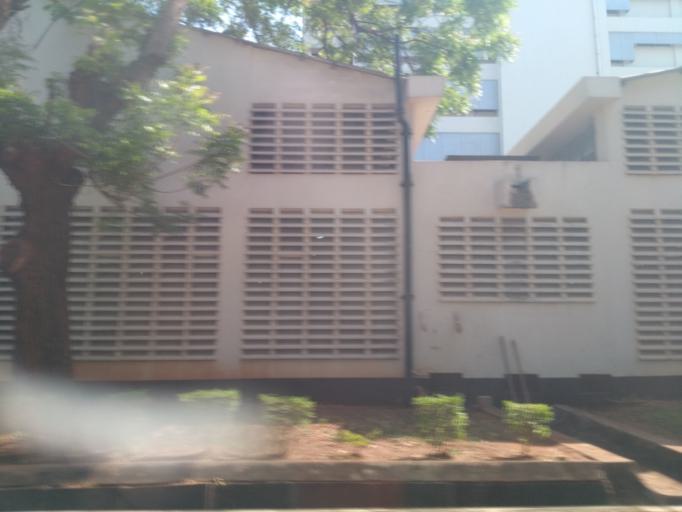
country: TZ
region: Dar es Salaam
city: Dar es Salaam
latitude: -6.8145
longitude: 39.2798
